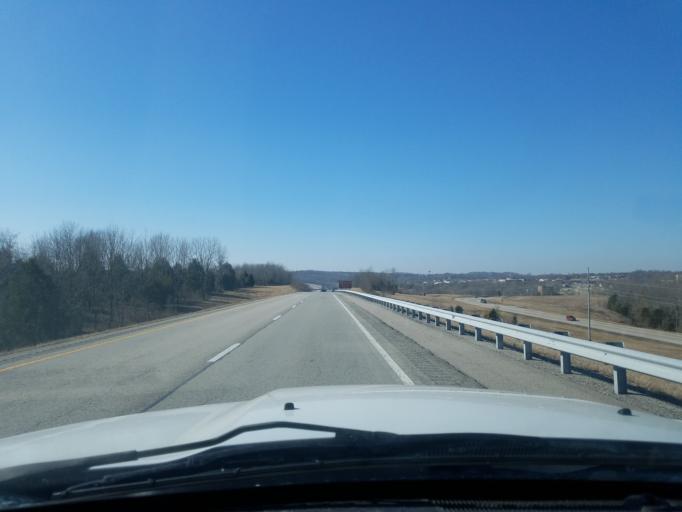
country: US
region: Kentucky
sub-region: Grayson County
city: Leitchfield
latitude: 37.4678
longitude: -86.2772
